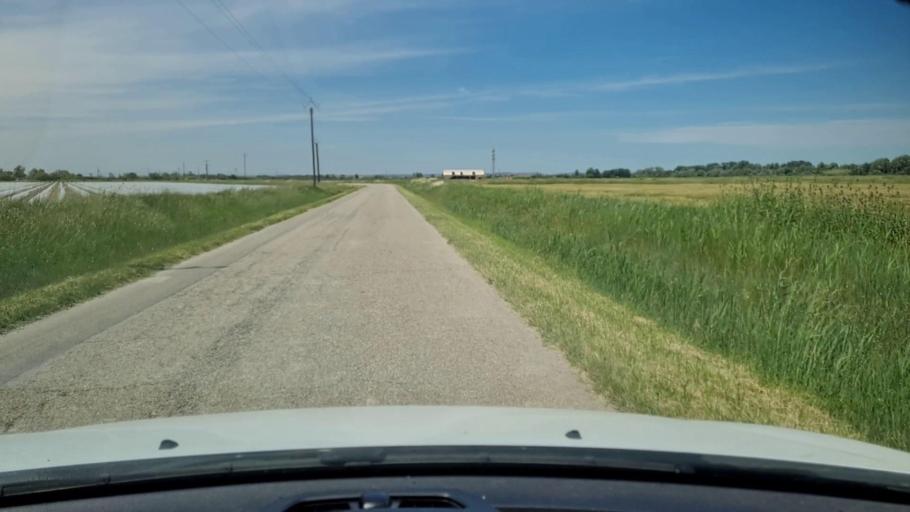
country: FR
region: Languedoc-Roussillon
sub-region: Departement du Gard
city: Saint-Gilles
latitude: 43.6074
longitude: 4.4320
